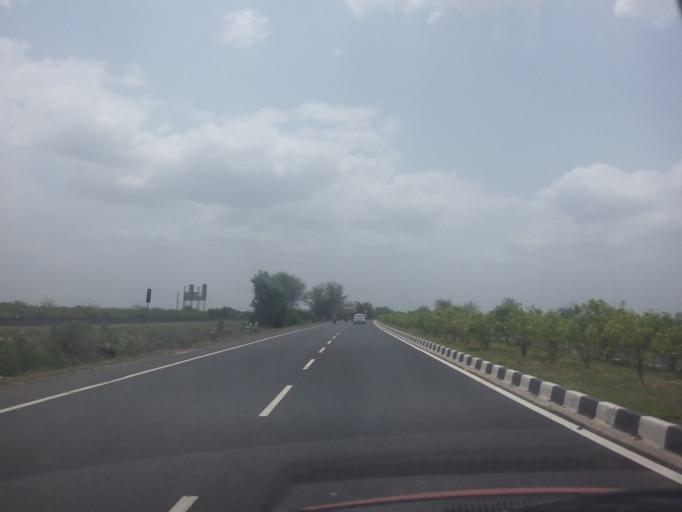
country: IN
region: Gujarat
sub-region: Ahmadabad
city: Sanand
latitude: 23.0800
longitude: 72.1884
